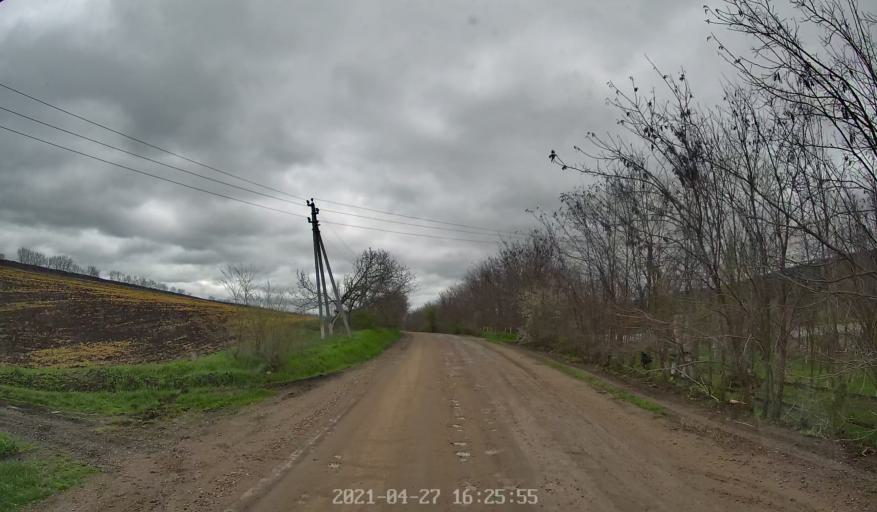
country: MD
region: Chisinau
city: Singera
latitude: 46.9822
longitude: 29.0222
